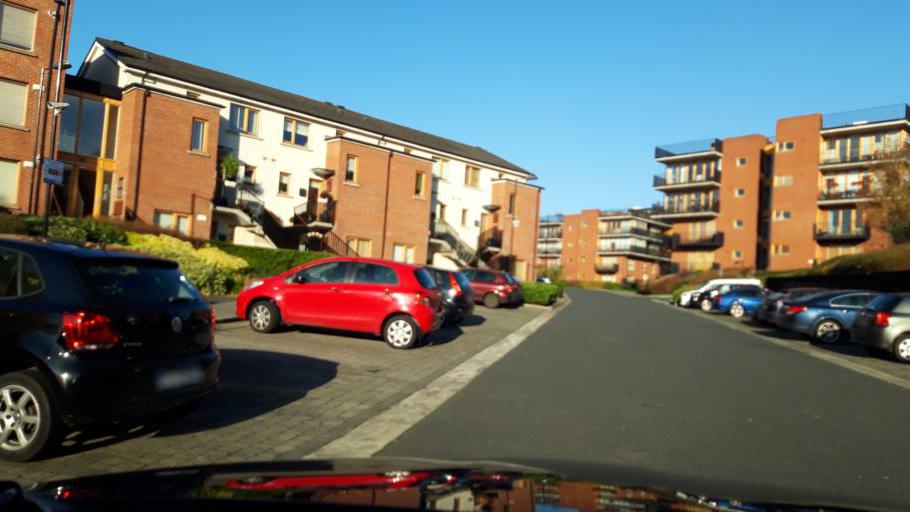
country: IE
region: Leinster
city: Glasnevin
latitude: 53.3761
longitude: -6.2772
